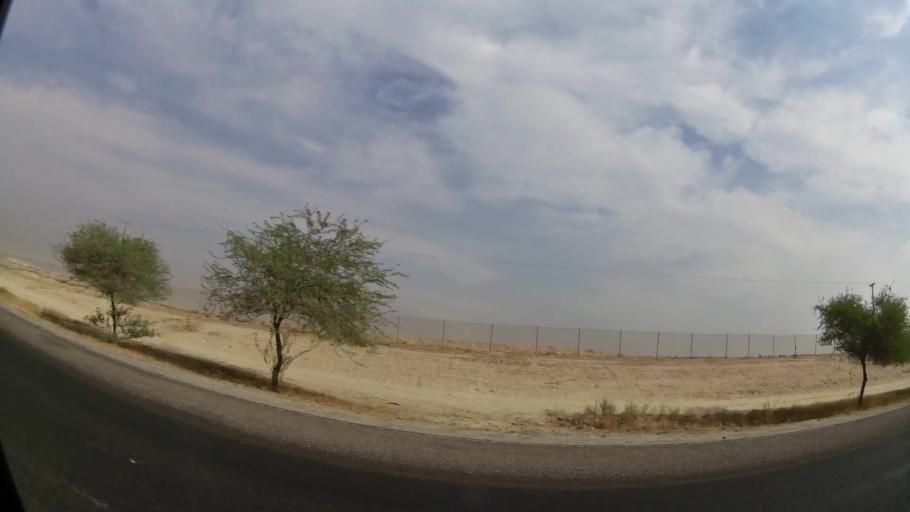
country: KW
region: Muhafazat al Jahra'
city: Al Jahra'
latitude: 29.2905
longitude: 47.7612
